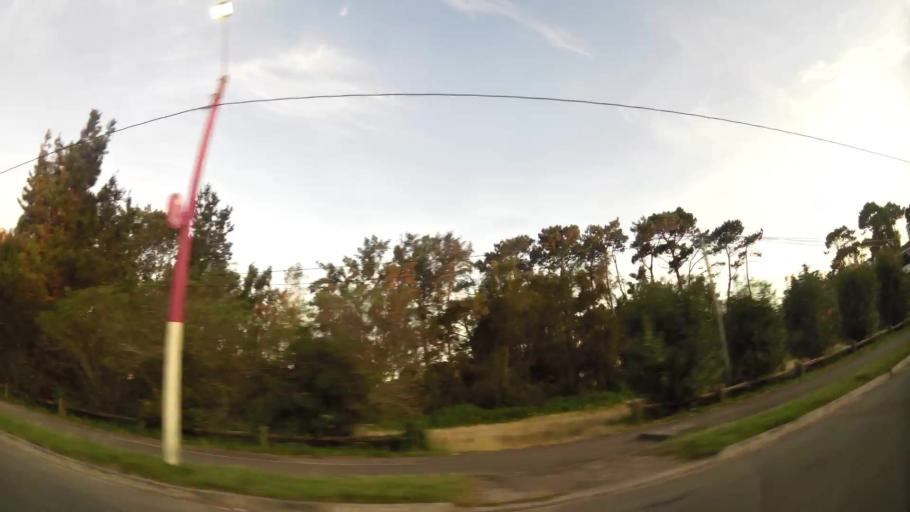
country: UY
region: Maldonado
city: Punta del Este
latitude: -34.9397
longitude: -54.9289
